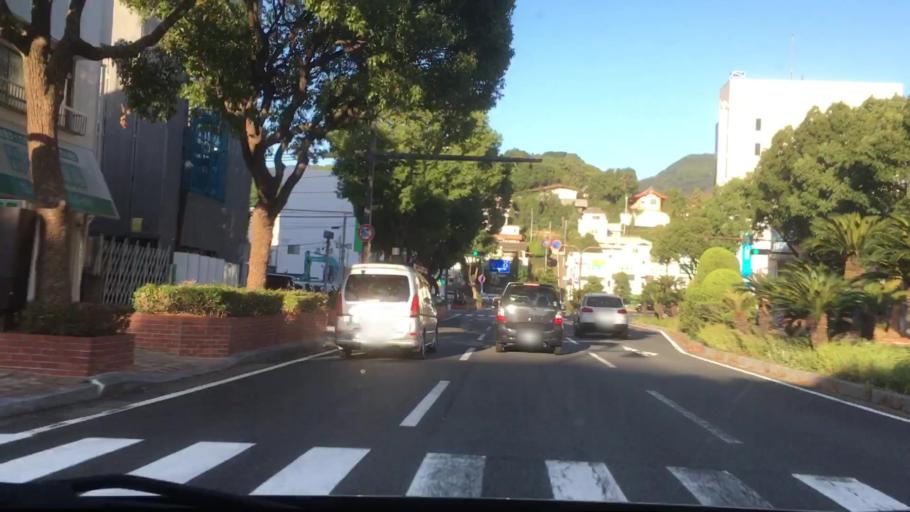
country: JP
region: Nagasaki
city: Sasebo
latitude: 33.1750
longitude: 129.7169
